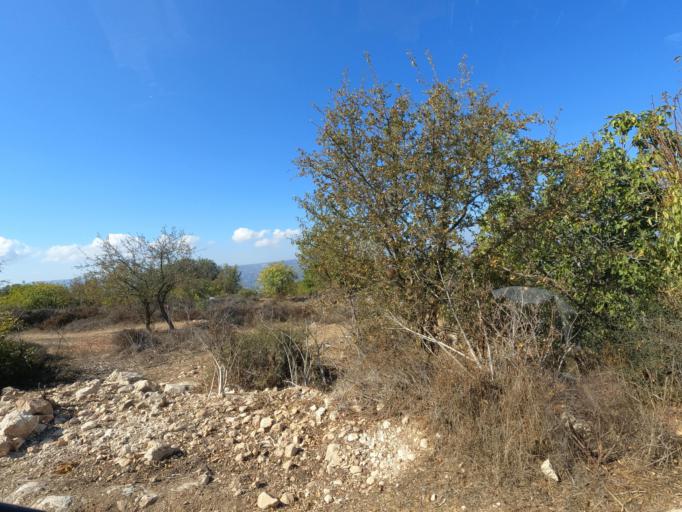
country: CY
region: Pafos
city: Polis
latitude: 34.9845
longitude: 32.5042
